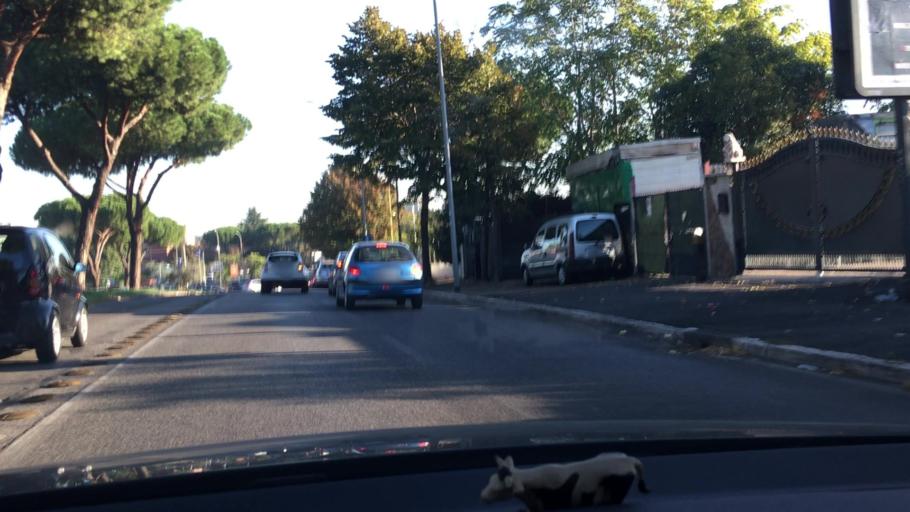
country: IT
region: Latium
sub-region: Citta metropolitana di Roma Capitale
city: Rome
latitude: 41.8726
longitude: 12.5691
